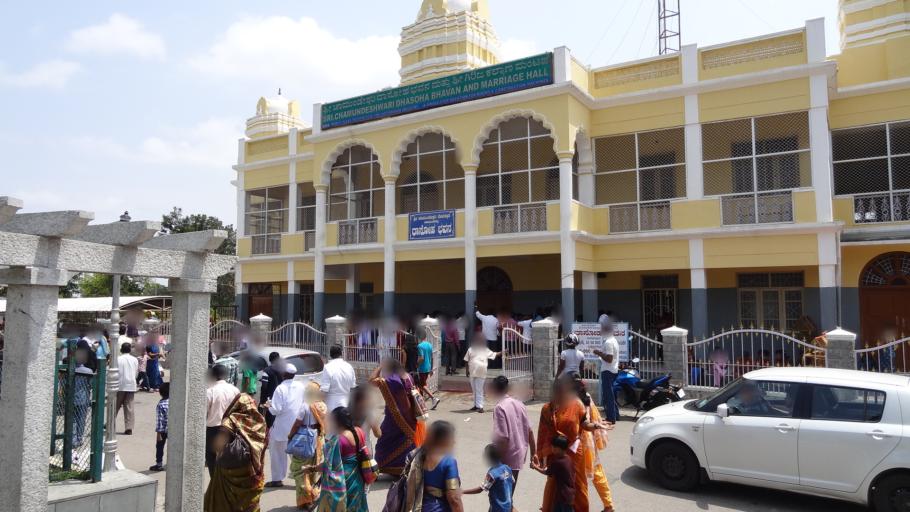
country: IN
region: Karnataka
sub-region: Mysore
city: Mysore
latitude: 12.2739
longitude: 76.6707
